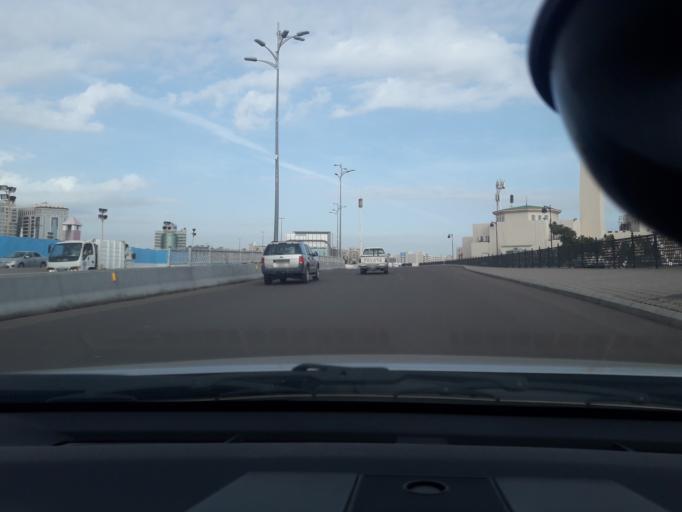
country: SA
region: Al Madinah al Munawwarah
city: Medina
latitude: 24.4708
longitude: 39.6188
